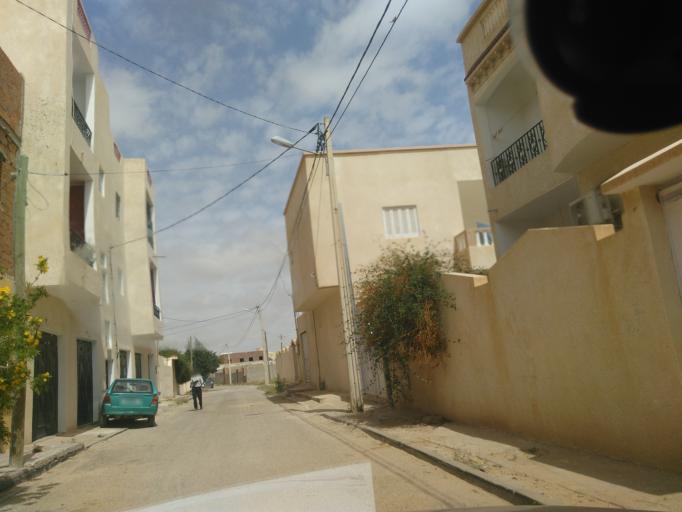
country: TN
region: Tataouine
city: Tataouine
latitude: 32.9533
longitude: 10.4667
